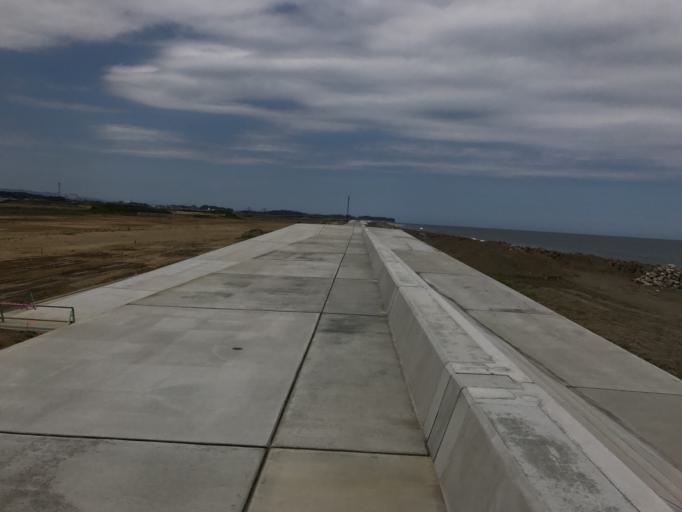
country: JP
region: Miyagi
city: Marumori
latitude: 37.7885
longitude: 140.9866
